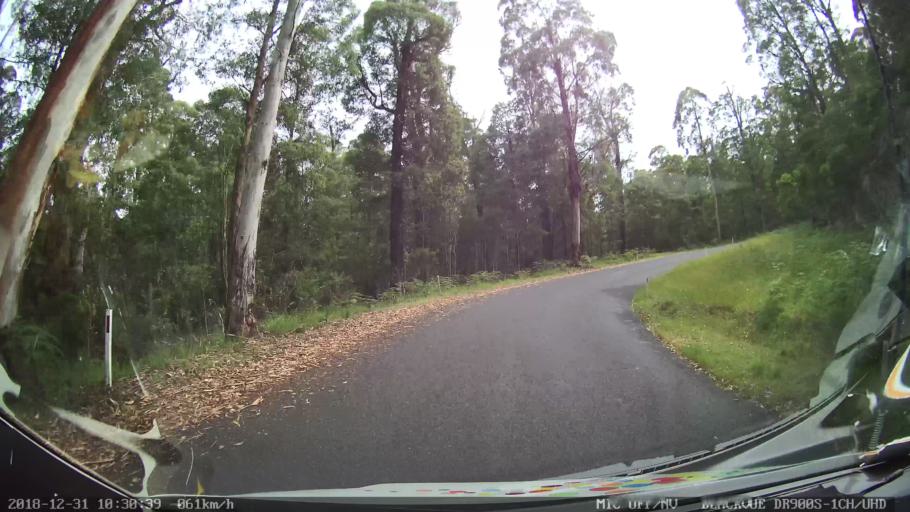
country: AU
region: New South Wales
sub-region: Snowy River
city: Jindabyne
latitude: -36.4613
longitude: 148.1506
